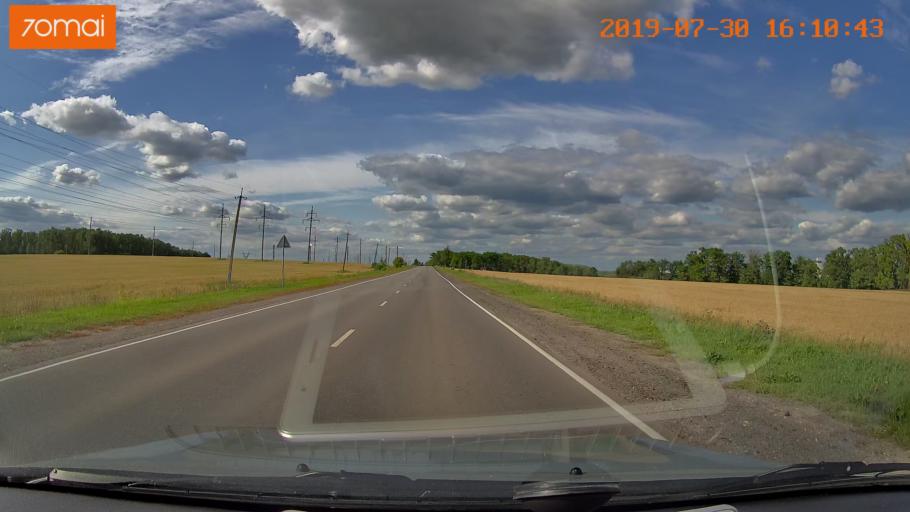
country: RU
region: Moskovskaya
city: Peski
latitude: 55.2658
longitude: 38.7151
